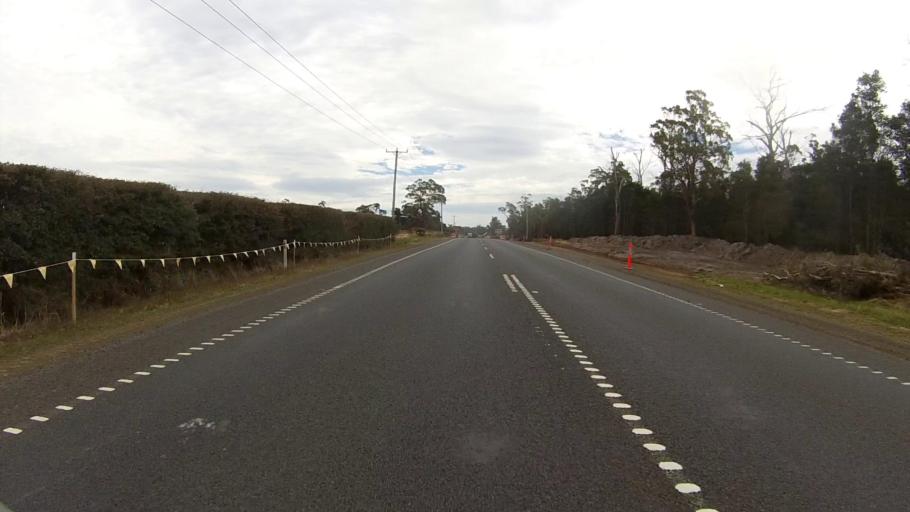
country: AU
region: Tasmania
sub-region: Northern Midlands
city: Evandale
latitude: -41.6031
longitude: 147.2158
